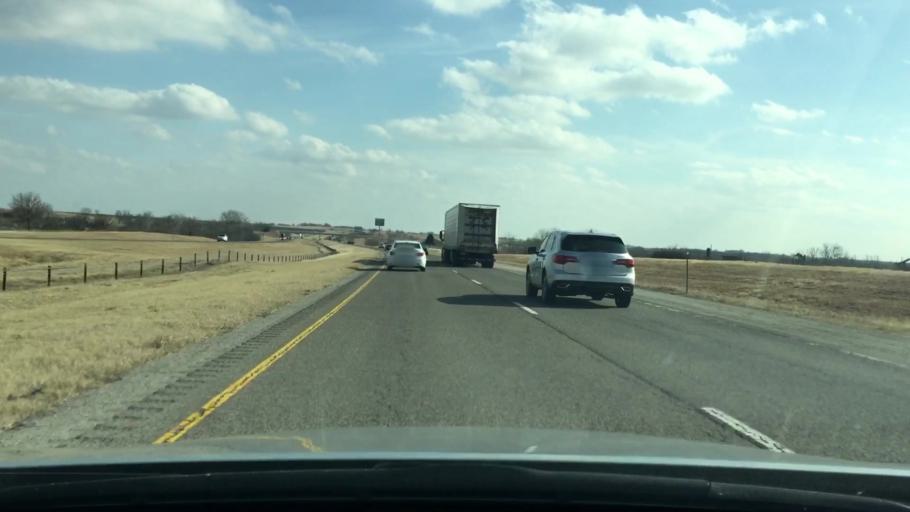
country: US
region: Oklahoma
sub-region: Garvin County
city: Maysville
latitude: 34.9045
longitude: -97.3508
